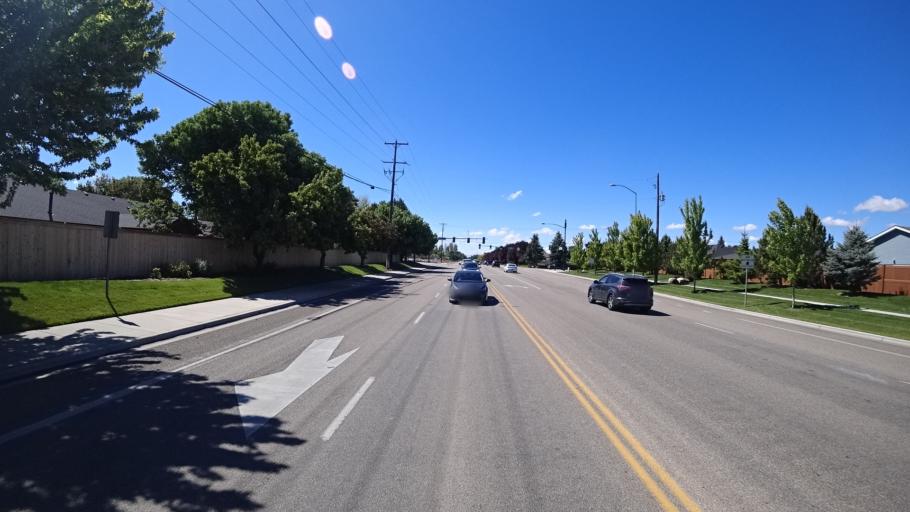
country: US
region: Idaho
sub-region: Ada County
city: Meridian
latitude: 43.6347
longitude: -116.3745
